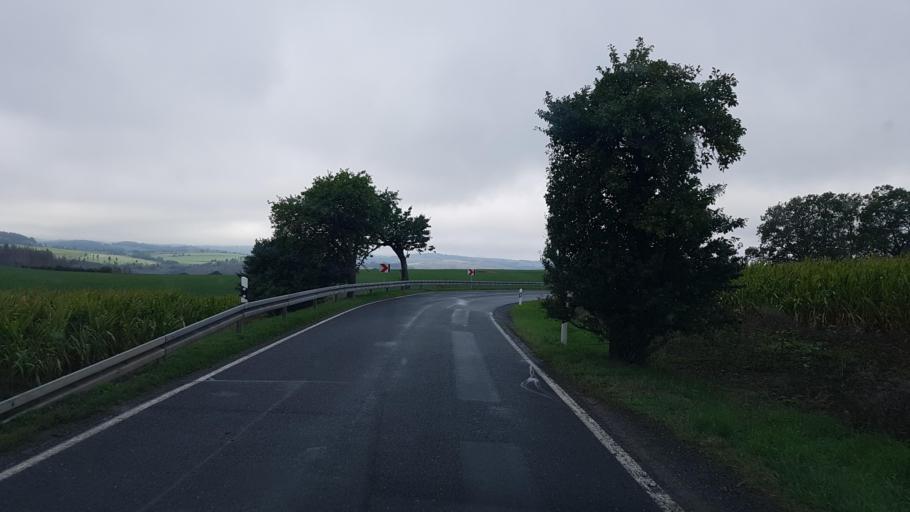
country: DE
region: Thuringia
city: Wurzbach
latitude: 50.5205
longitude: 11.5428
